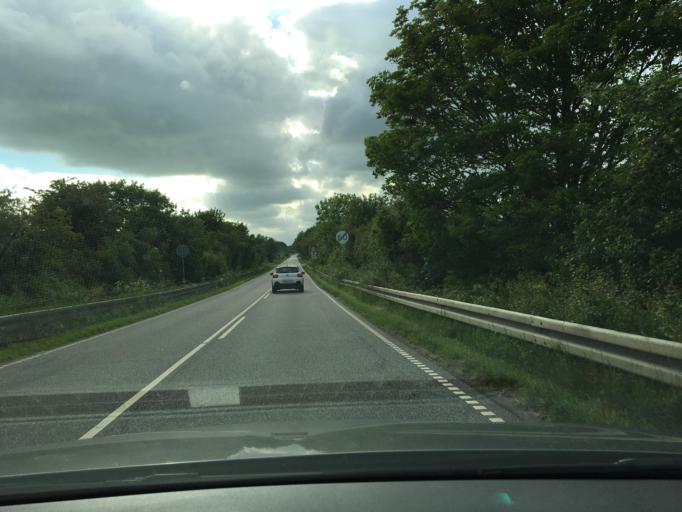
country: DK
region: Central Jutland
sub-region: Arhus Kommune
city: Logten
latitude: 56.2886
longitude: 10.3090
